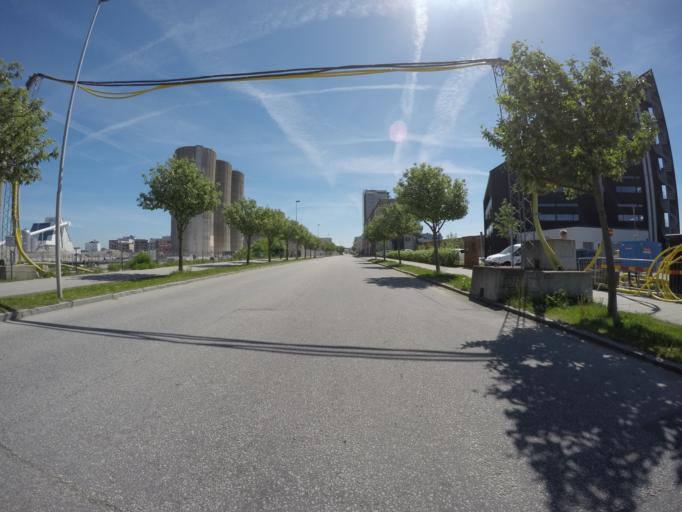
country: SE
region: Skane
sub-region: Malmo
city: Bunkeflostrand
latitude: 55.5882
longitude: 12.9247
